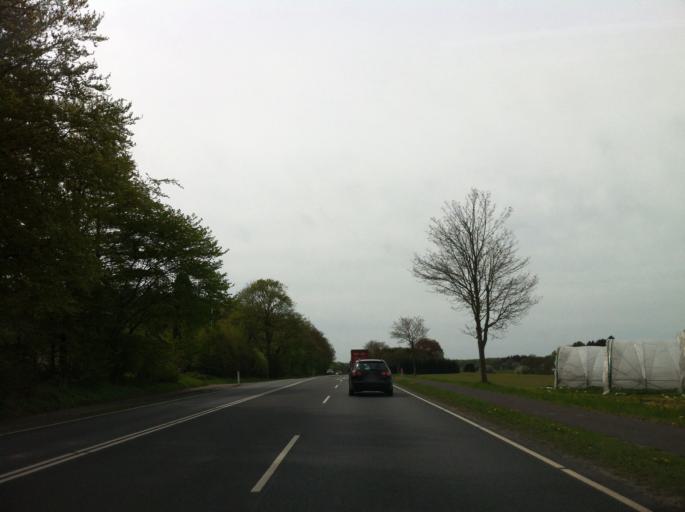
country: DK
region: Zealand
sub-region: Lejre Kommune
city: Osted
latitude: 55.5365
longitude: 11.9239
